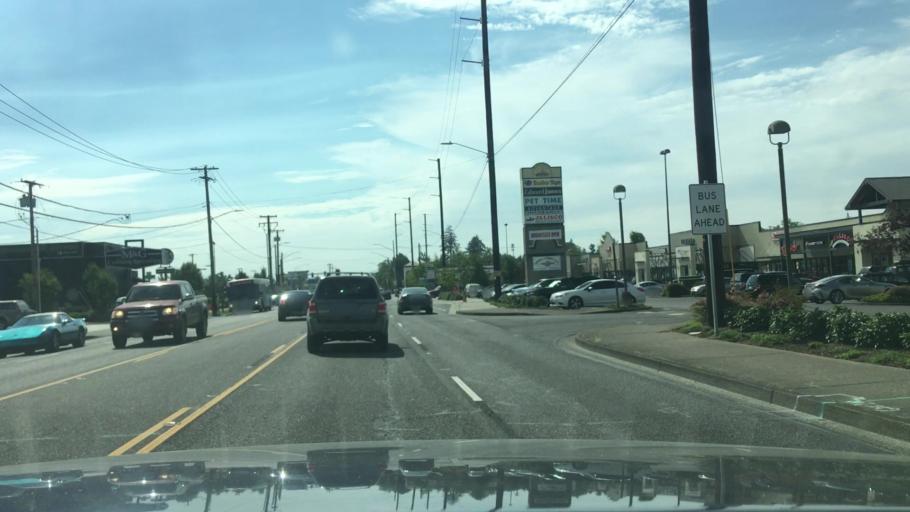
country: US
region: Oregon
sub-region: Lane County
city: Eugene
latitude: 44.0480
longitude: -123.1376
